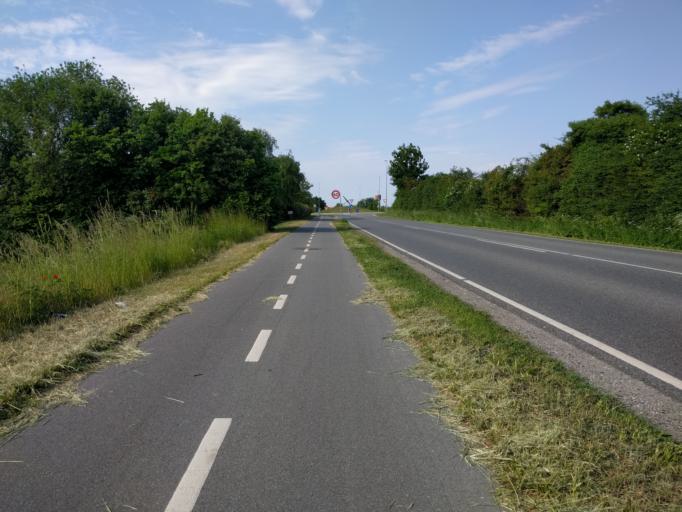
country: DK
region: South Denmark
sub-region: Kerteminde Kommune
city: Kerteminde
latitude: 55.4374
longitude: 10.6553
